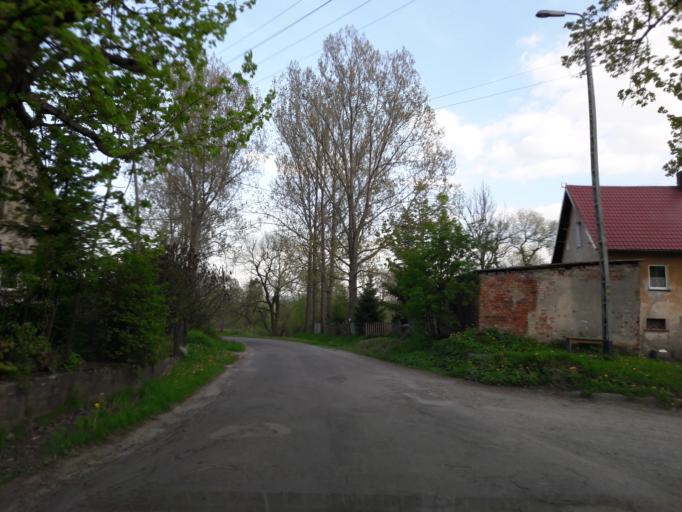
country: PL
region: Lower Silesian Voivodeship
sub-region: Powiat klodzki
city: Duszniki-Zdroj
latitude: 50.4286
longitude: 16.3613
